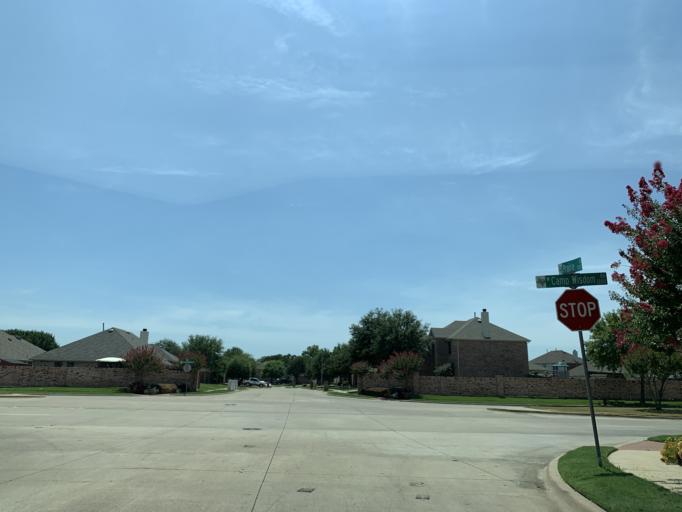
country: US
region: Texas
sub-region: Dallas County
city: Cedar Hill
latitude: 32.6457
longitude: -97.0213
